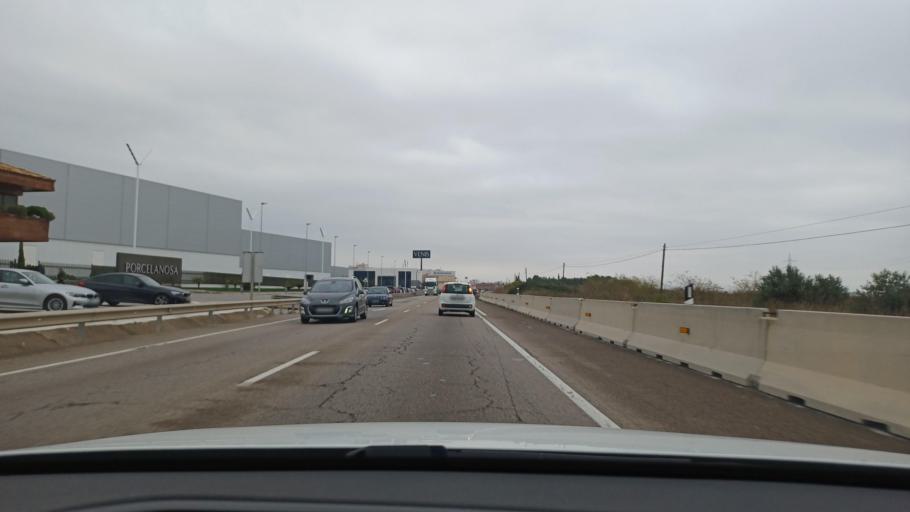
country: ES
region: Valencia
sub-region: Provincia de Castello
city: Vila-real
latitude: 39.9196
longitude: -0.1089
